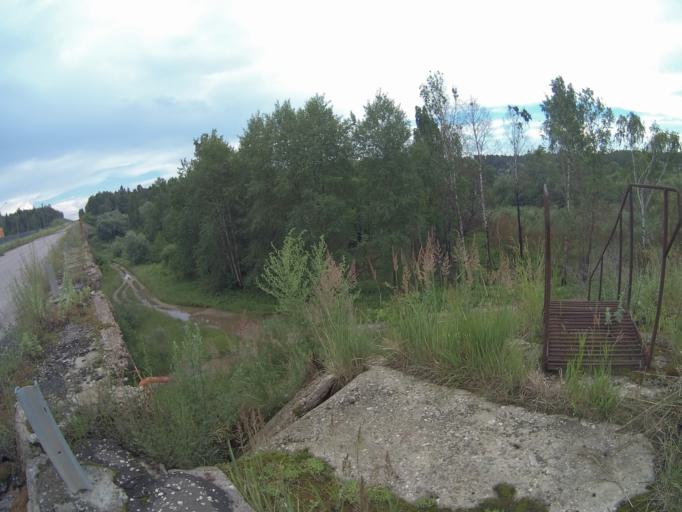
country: RU
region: Vladimir
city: Kameshkovo
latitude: 56.1969
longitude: 40.9047
